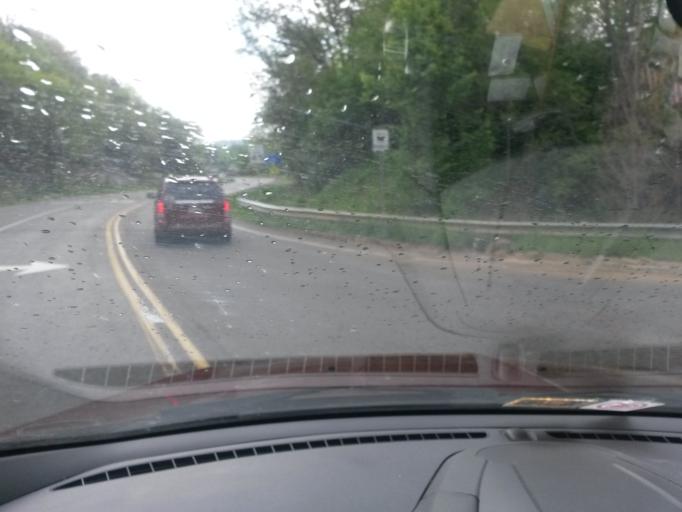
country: US
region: Virginia
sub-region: Botetourt County
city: Cloverdale
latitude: 37.3634
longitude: -79.9051
